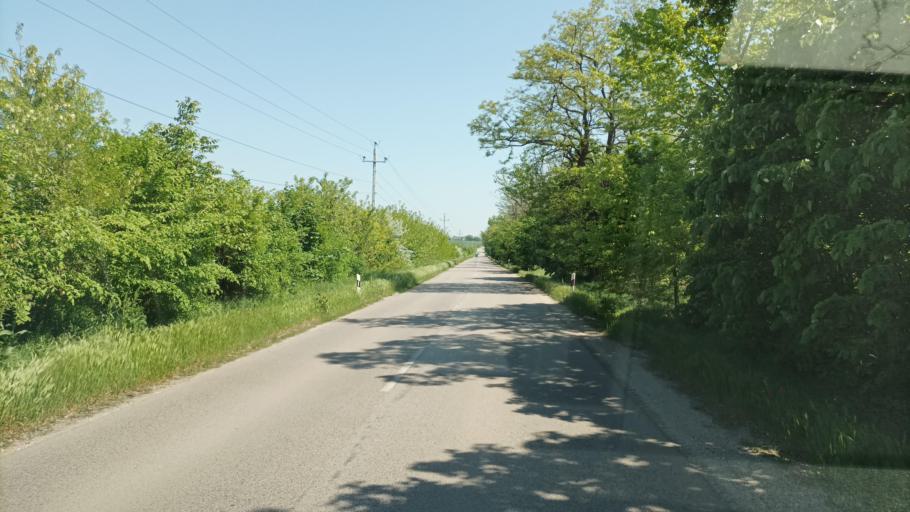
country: HU
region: Pest
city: Uri
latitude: 47.4261
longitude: 19.5258
